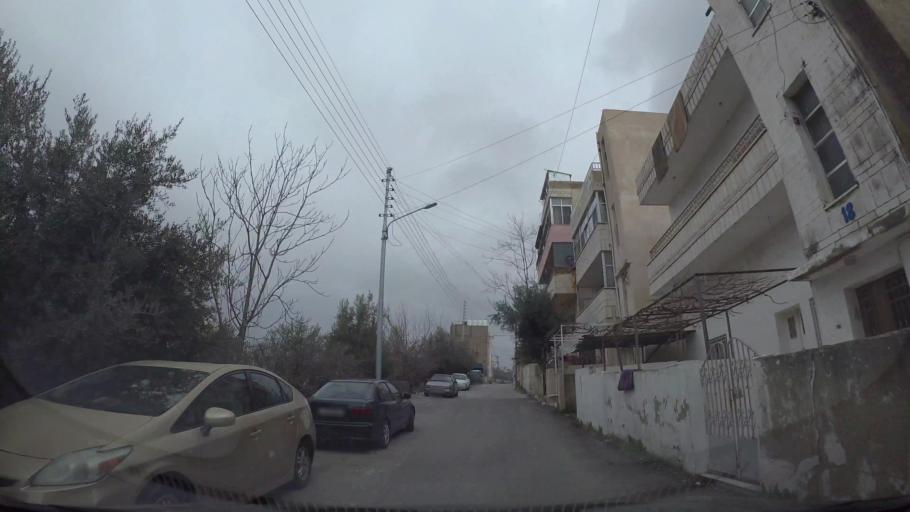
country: JO
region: Amman
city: Wadi as Sir
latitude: 31.9468
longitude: 35.8151
